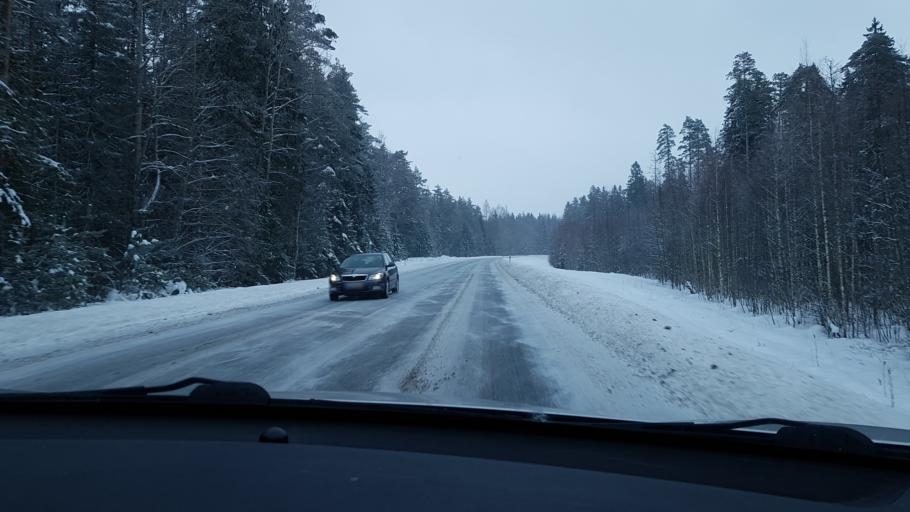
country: EE
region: Jaervamaa
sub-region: Tueri vald
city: Sarevere
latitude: 58.7384
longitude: 25.3009
